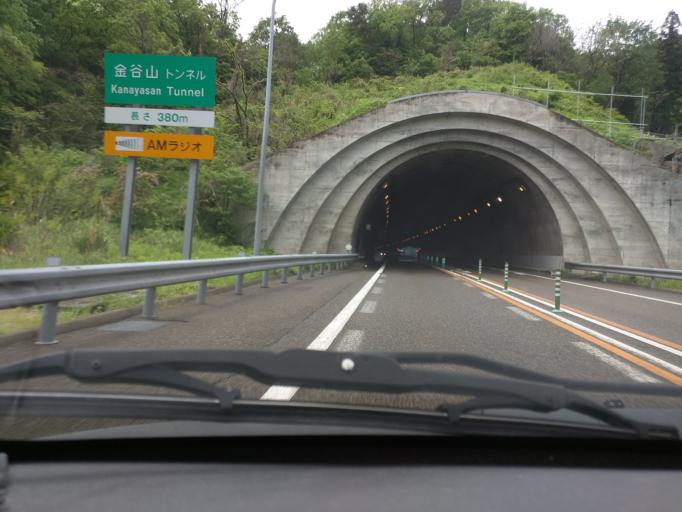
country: JP
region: Niigata
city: Joetsu
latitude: 37.1063
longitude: 138.2198
